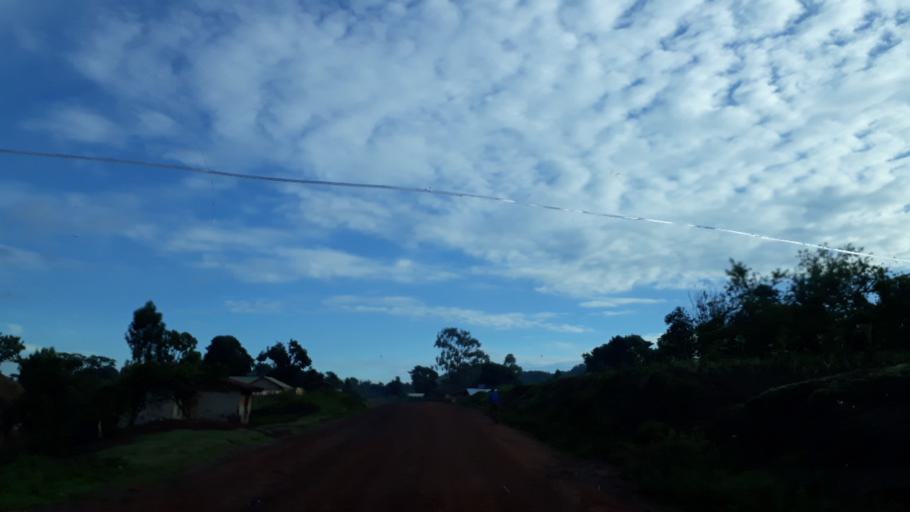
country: UG
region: Northern Region
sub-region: Zombo District
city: Paidha
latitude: 2.2366
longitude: 30.8608
